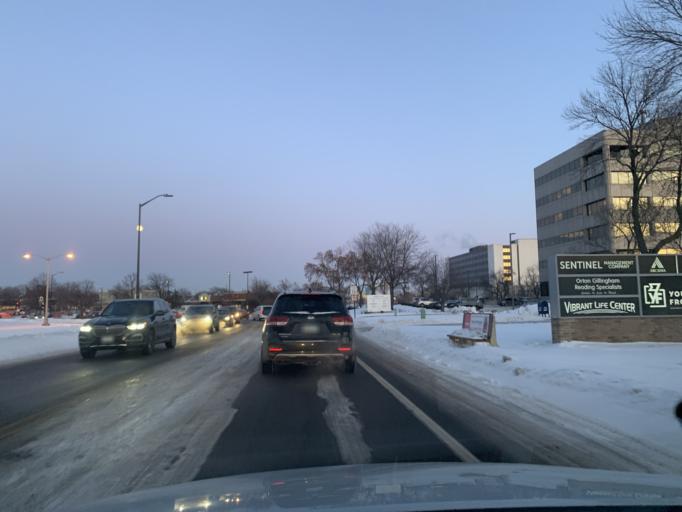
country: US
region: Minnesota
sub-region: Hennepin County
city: Edina
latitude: 44.8632
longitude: -93.3561
